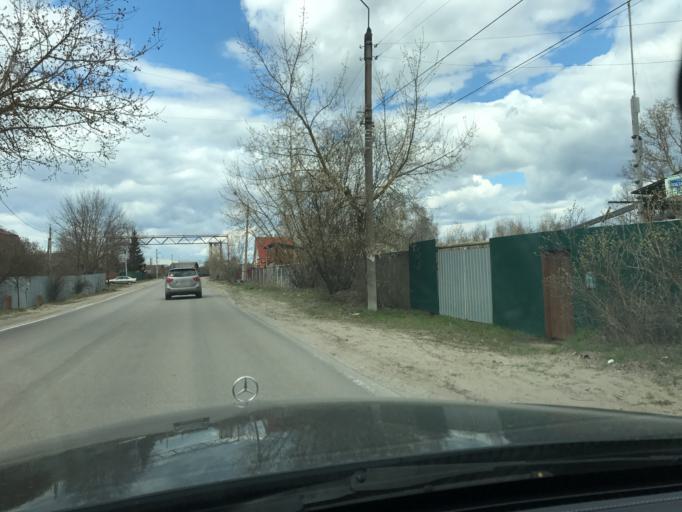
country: RU
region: Vladimir
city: Pokrov
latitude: 55.8939
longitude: 39.2098
